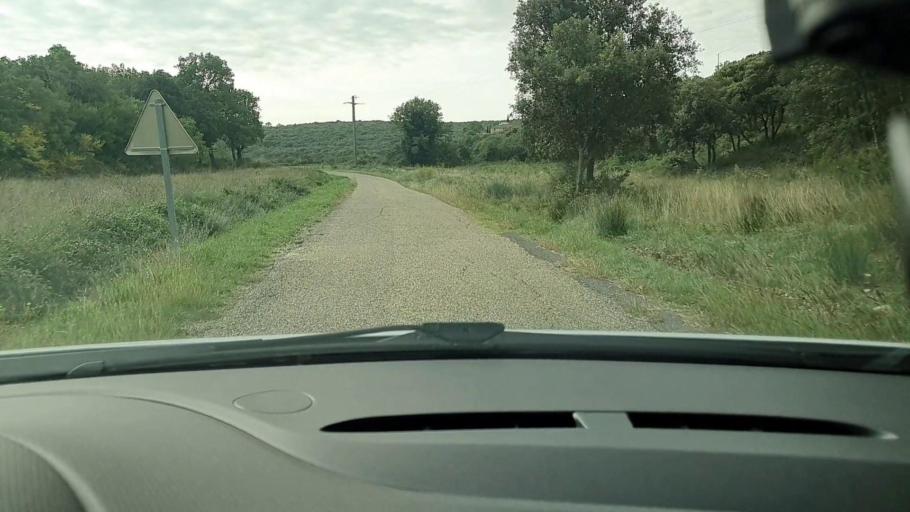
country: FR
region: Languedoc-Roussillon
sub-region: Departement du Gard
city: Montaren-et-Saint-Mediers
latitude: 44.1076
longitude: 4.3028
